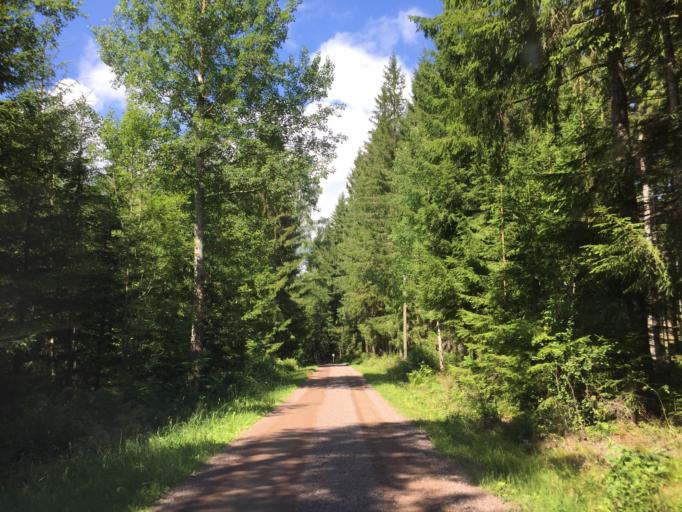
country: SE
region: OEstergoetland
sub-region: Odeshogs Kommun
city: OEdeshoeg
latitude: 58.1775
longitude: 14.7162
